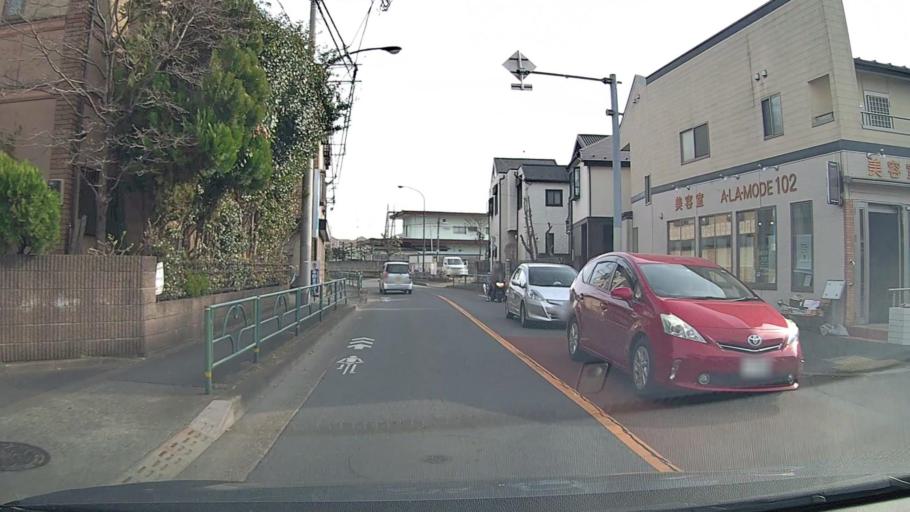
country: JP
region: Tokyo
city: Nishi-Tokyo-shi
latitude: 35.7582
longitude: 139.5778
